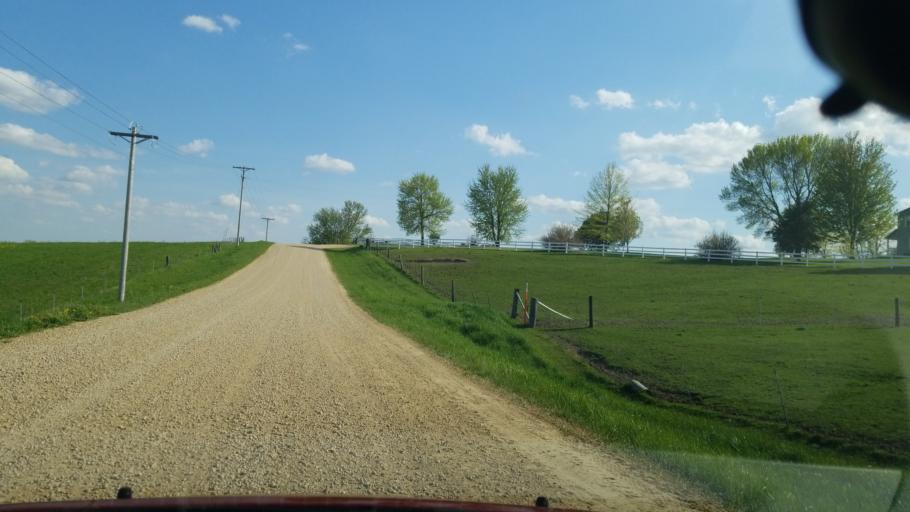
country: US
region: Iowa
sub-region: Jackson County
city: Maquoketa
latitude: 42.2037
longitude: -90.7294
